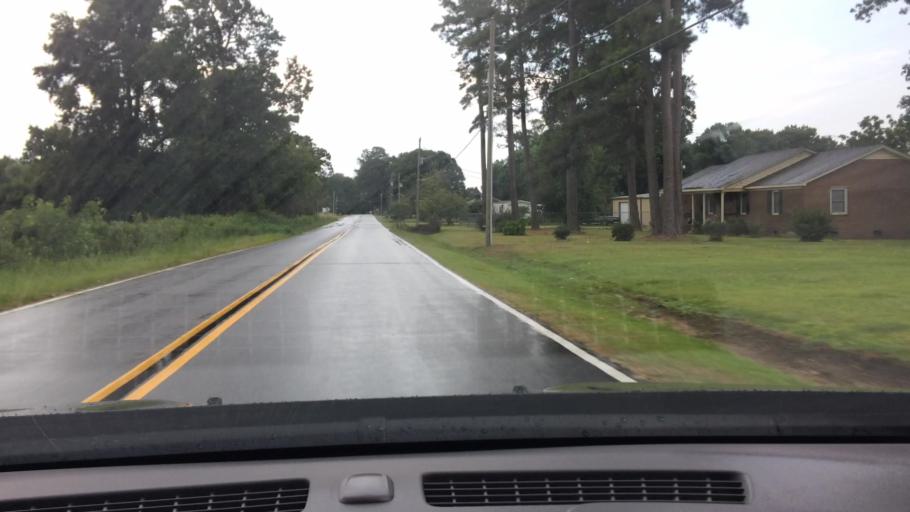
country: US
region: North Carolina
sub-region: Pitt County
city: Ayden
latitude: 35.4915
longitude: -77.3775
